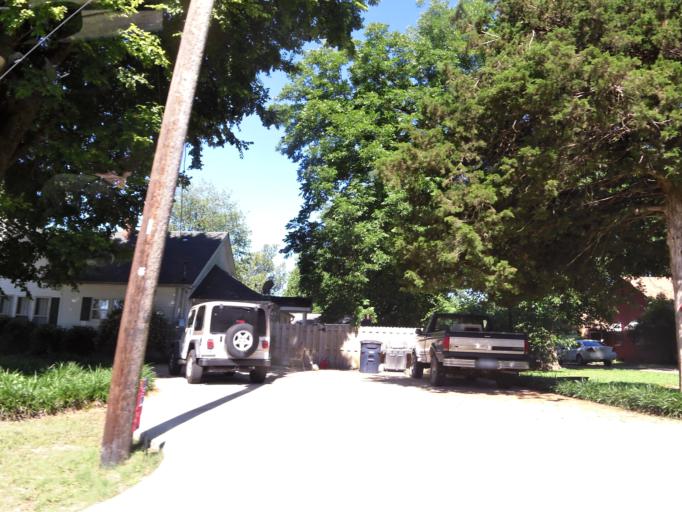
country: US
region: Arkansas
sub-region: Clay County
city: Piggott
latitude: 36.3862
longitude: -90.1943
